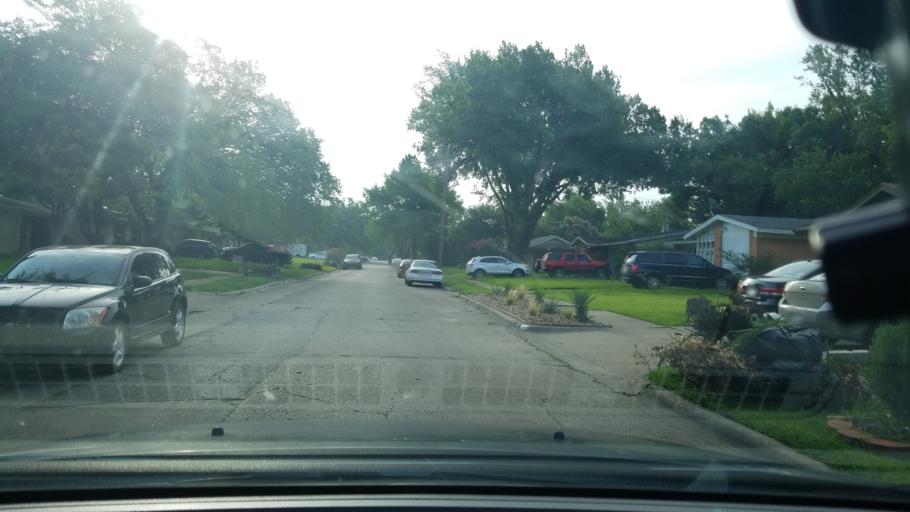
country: US
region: Texas
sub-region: Dallas County
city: Garland
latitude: 32.8303
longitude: -96.6708
